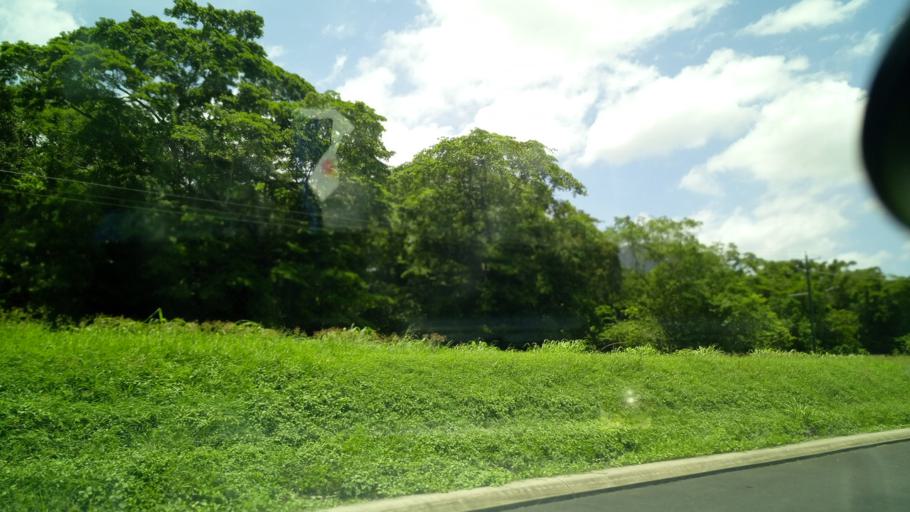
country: AU
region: Queensland
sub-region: Cairns
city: Woree
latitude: -16.9410
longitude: 145.7466
